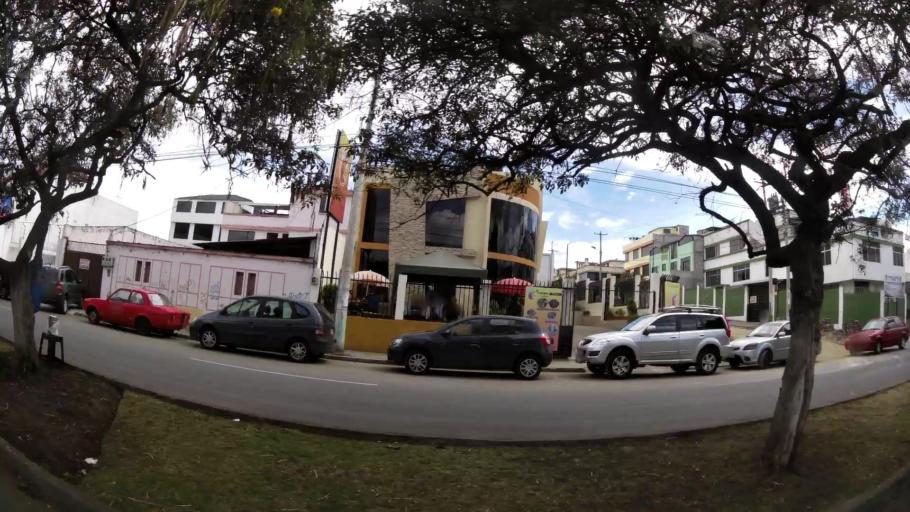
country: EC
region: Tungurahua
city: Ambato
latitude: -1.2514
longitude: -78.6239
